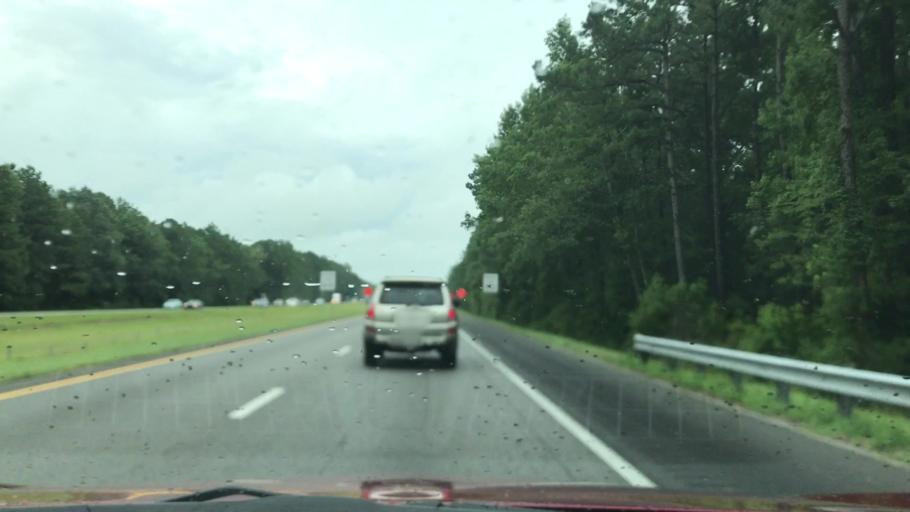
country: US
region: South Carolina
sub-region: Dorchester County
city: Ridgeville
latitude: 33.1280
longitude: -80.2920
